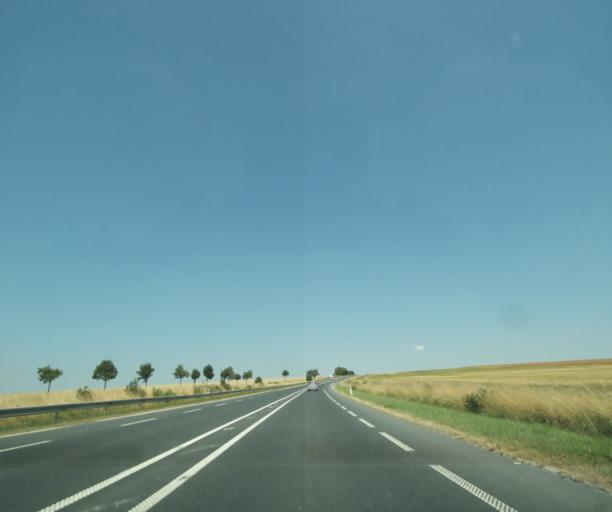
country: FR
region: Champagne-Ardenne
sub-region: Departement de la Marne
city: Mourmelon-le-Grand
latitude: 49.0724
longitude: 4.2902
